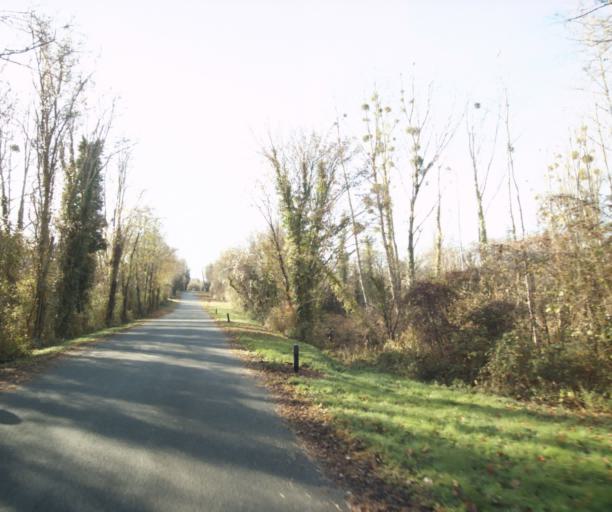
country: FR
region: Poitou-Charentes
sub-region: Departement de la Charente-Maritime
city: Chaniers
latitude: 45.7544
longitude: -0.5015
